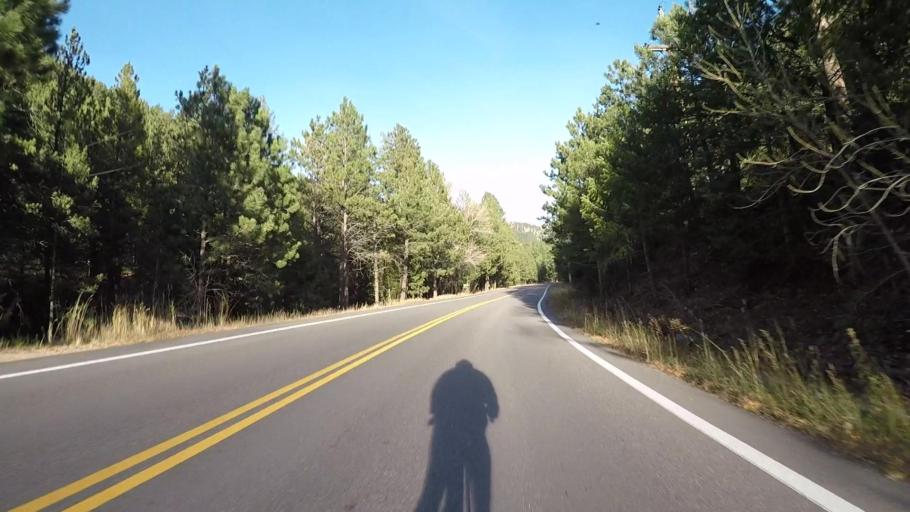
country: US
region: Colorado
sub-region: Boulder County
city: Boulder
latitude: 40.0896
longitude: -105.3614
